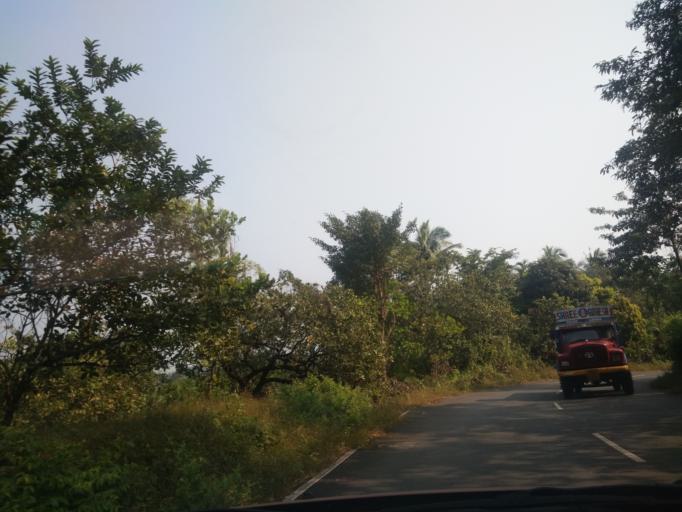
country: IN
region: Goa
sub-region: North Goa
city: Palle
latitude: 15.4827
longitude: 74.1298
